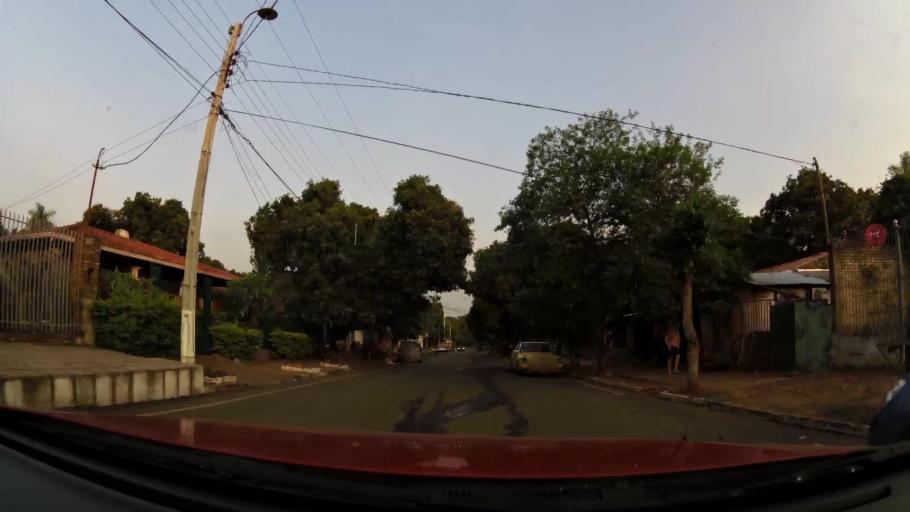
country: PY
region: Central
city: Lambare
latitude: -25.3521
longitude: -57.5955
